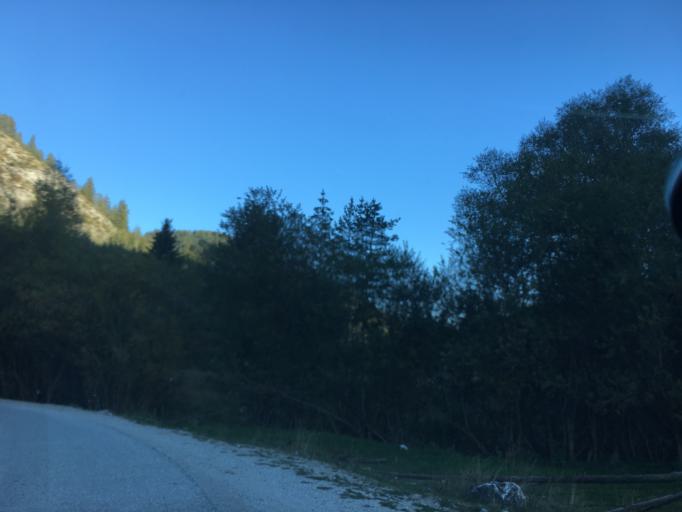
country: BG
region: Smolyan
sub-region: Obshtina Borino
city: Borino
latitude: 41.5858
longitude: 24.3894
